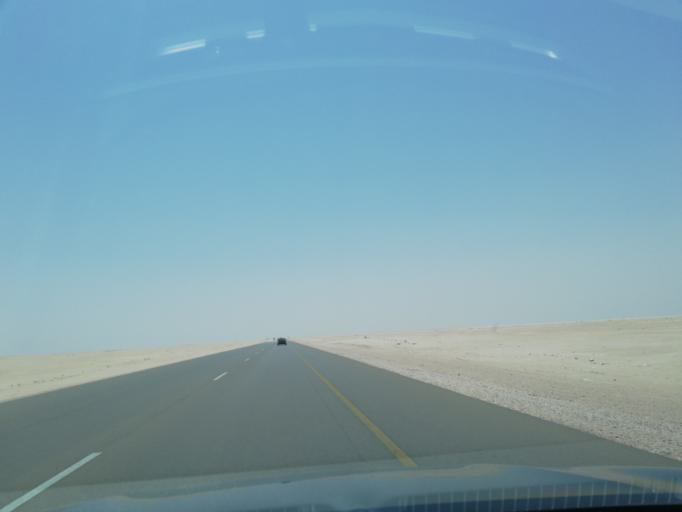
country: OM
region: Al Wusta
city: Hayma'
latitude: 20.1707
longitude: 56.5225
